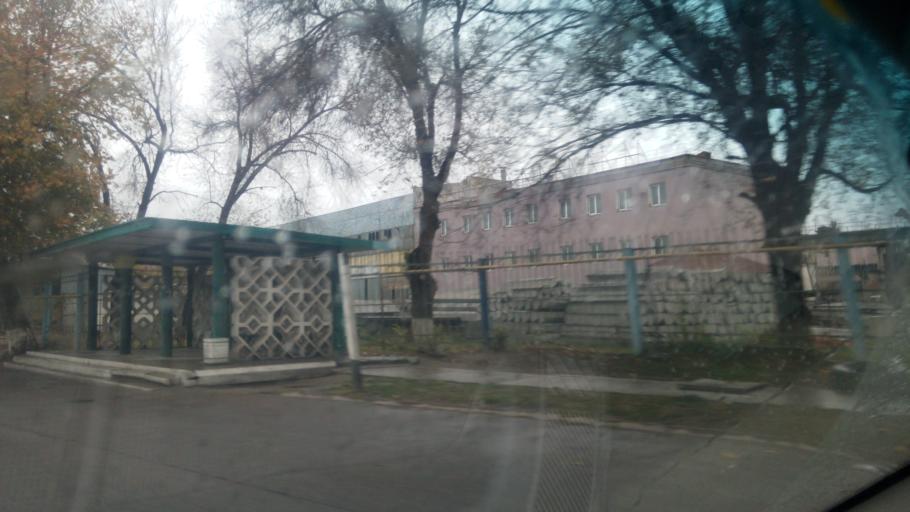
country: UZ
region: Toshkent Shahri
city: Bektemir
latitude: 41.2505
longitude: 69.3542
